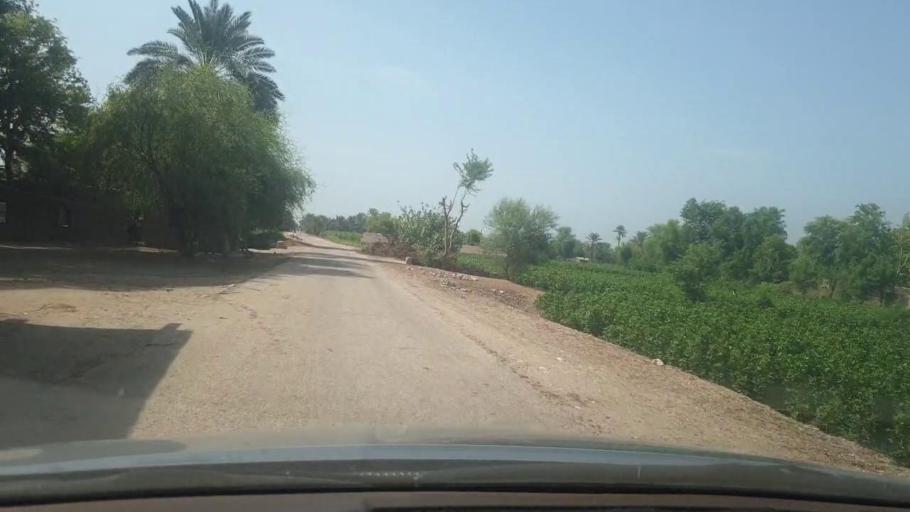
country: PK
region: Sindh
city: Ranipur
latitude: 27.2726
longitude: 68.5816
